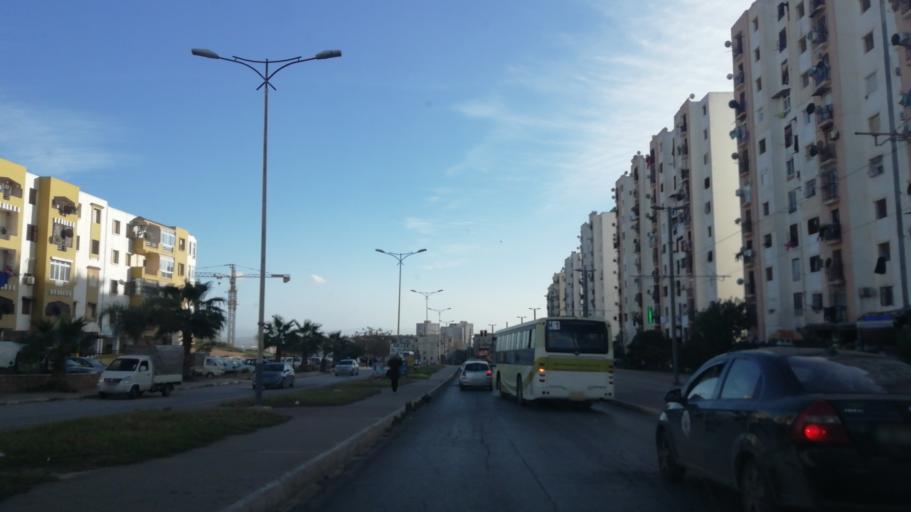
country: DZ
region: Oran
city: Bir el Djir
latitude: 35.7019
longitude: -0.5690
